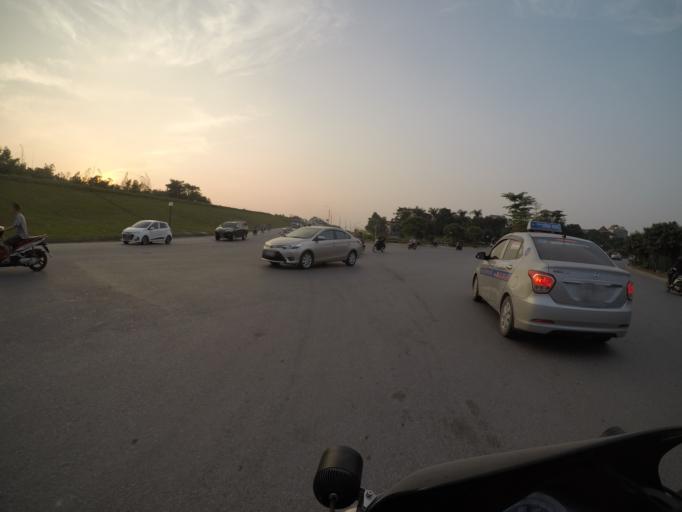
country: VN
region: Ha Noi
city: Hoan Kiem
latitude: 21.0313
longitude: 105.8796
